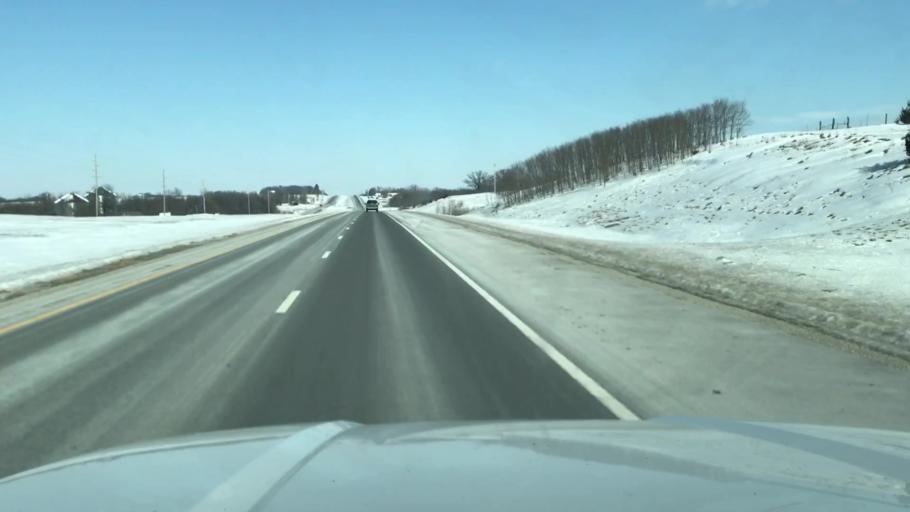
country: US
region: Missouri
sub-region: Nodaway County
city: Maryville
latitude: 40.1914
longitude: -94.8678
